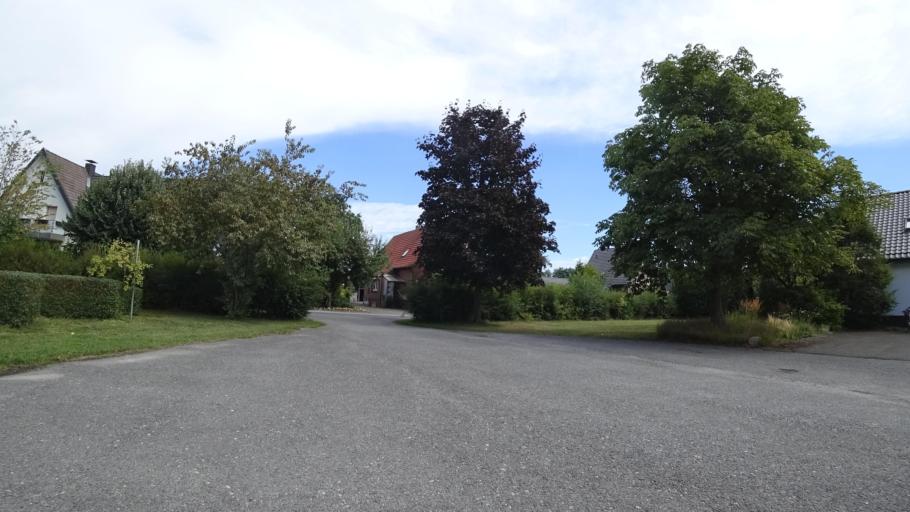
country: DE
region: North Rhine-Westphalia
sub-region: Regierungsbezirk Detmold
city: Steinhagen
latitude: 51.9511
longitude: 8.4137
